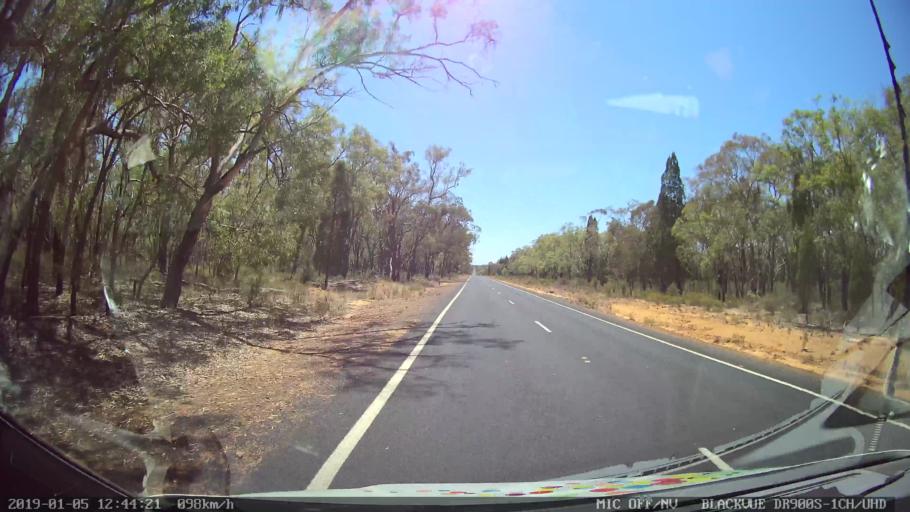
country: AU
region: New South Wales
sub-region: Warrumbungle Shire
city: Coonabarabran
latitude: -31.1387
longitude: 149.5361
